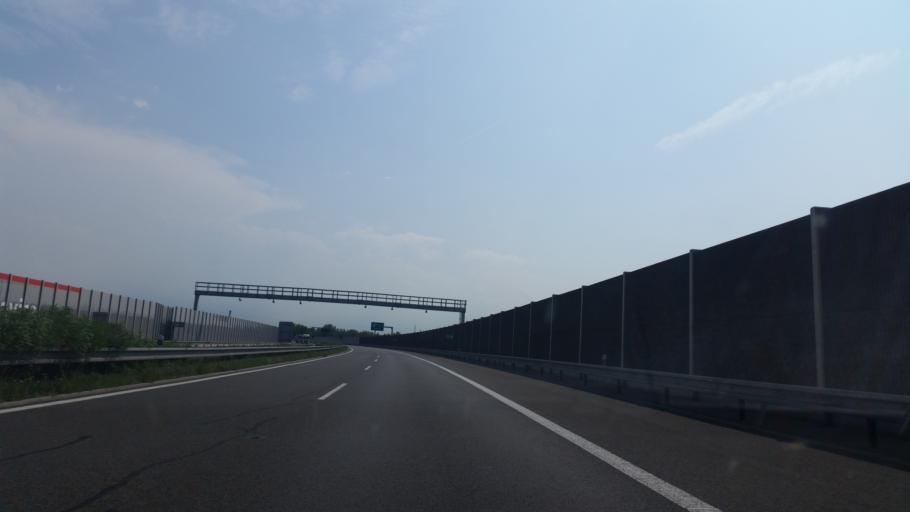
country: PL
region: Silesian Voivodeship
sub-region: Powiat raciborski
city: Chalupki
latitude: 49.8968
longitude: 18.3033
